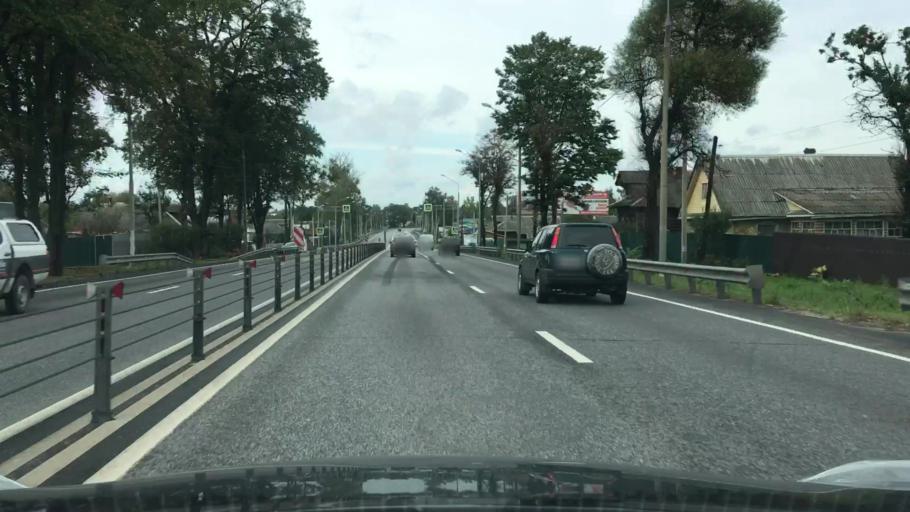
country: RU
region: Tverskaya
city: Zavidovo
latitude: 56.5155
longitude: 36.5359
